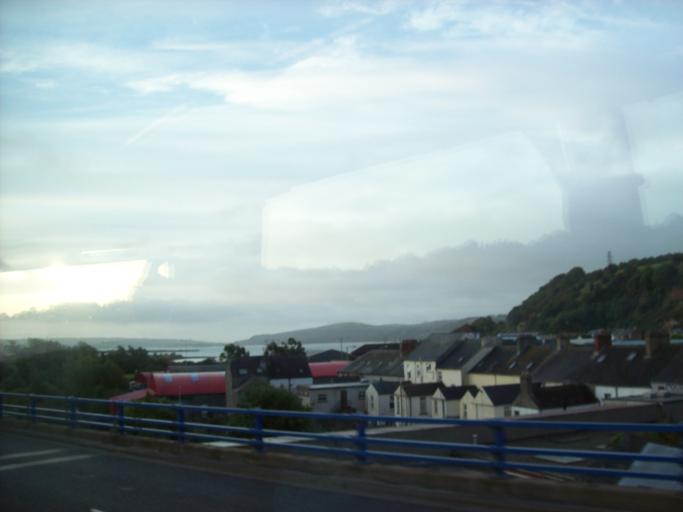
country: GB
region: Northern Ireland
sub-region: Larne District
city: Larne
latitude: 54.8507
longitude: -5.8261
